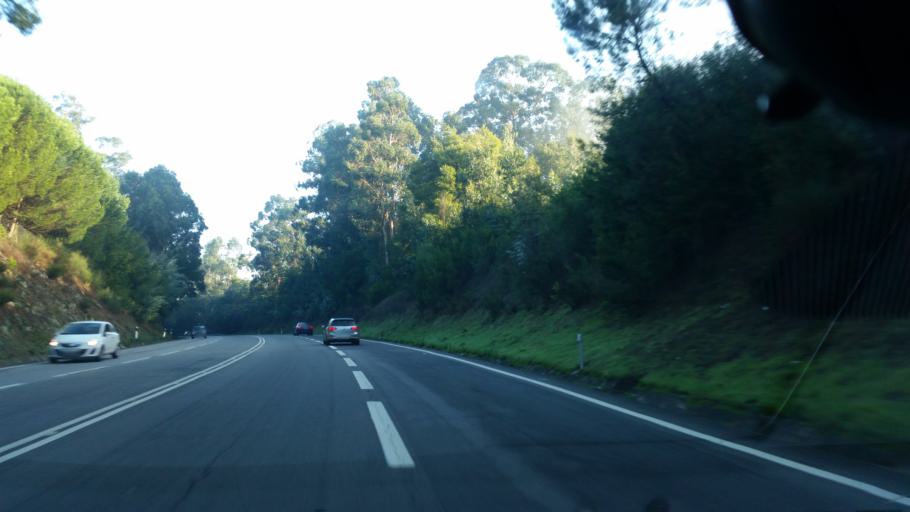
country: PT
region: Porto
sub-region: Santo Tirso
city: Sao Miguel do Couto
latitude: 41.3346
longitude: -8.4674
